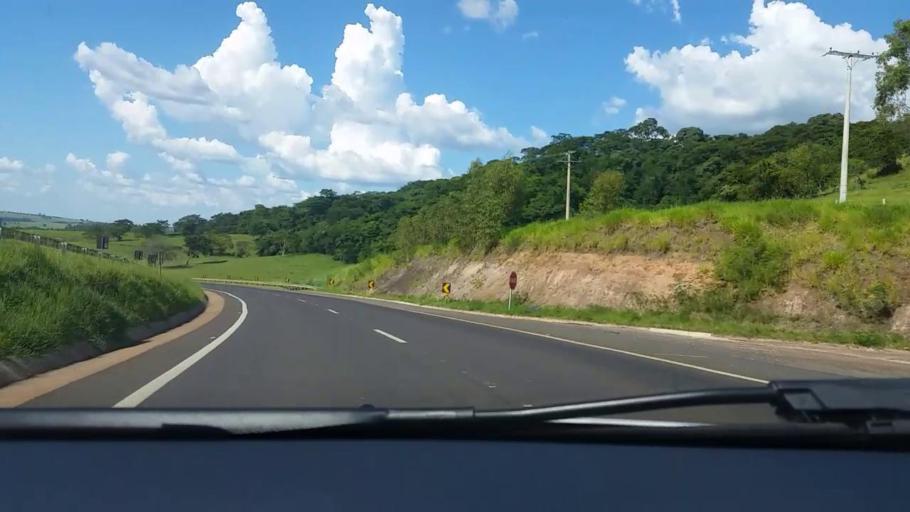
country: BR
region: Sao Paulo
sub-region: Bauru
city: Bauru
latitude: -22.4350
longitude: -49.1342
